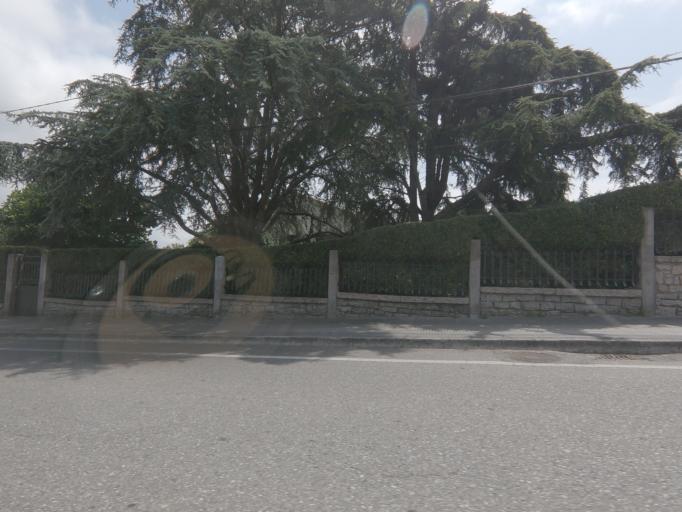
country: ES
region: Galicia
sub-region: Provincia de Pontevedra
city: A Guarda
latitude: 41.9076
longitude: -8.8607
